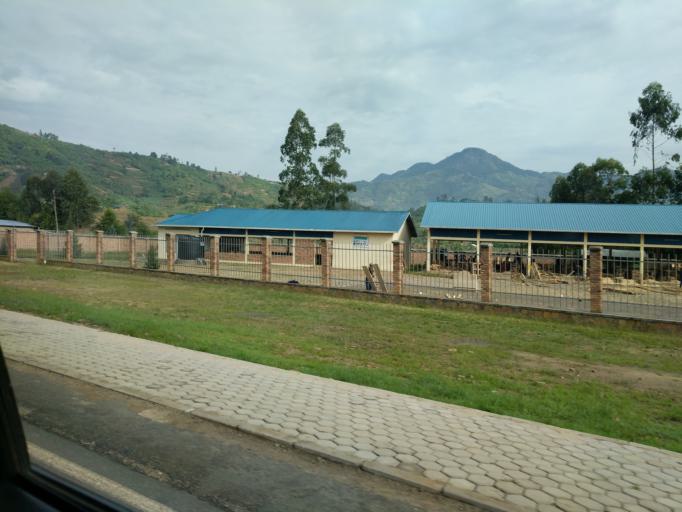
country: RW
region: Northern Province
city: Musanze
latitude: -1.6563
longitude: 29.8237
